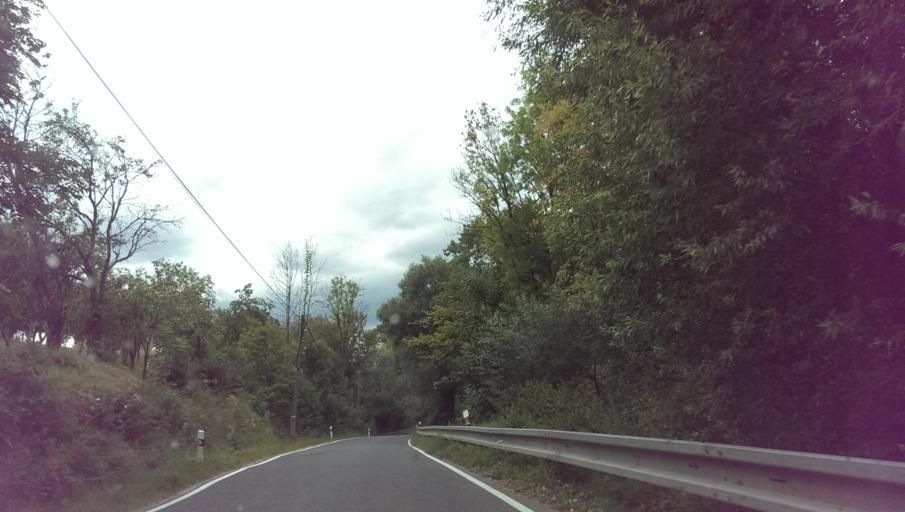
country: CZ
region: South Moravian
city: Velka nad Velickou
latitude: 48.8684
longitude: 17.5886
